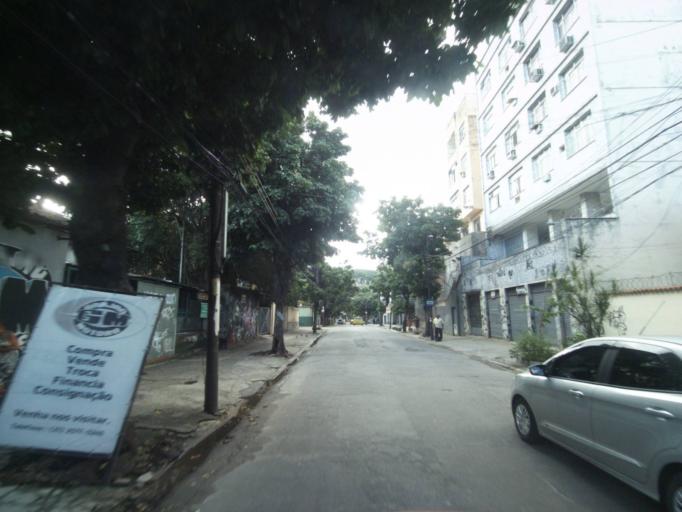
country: BR
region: Rio de Janeiro
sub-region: Rio De Janeiro
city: Rio de Janeiro
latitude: -22.9193
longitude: -43.2599
